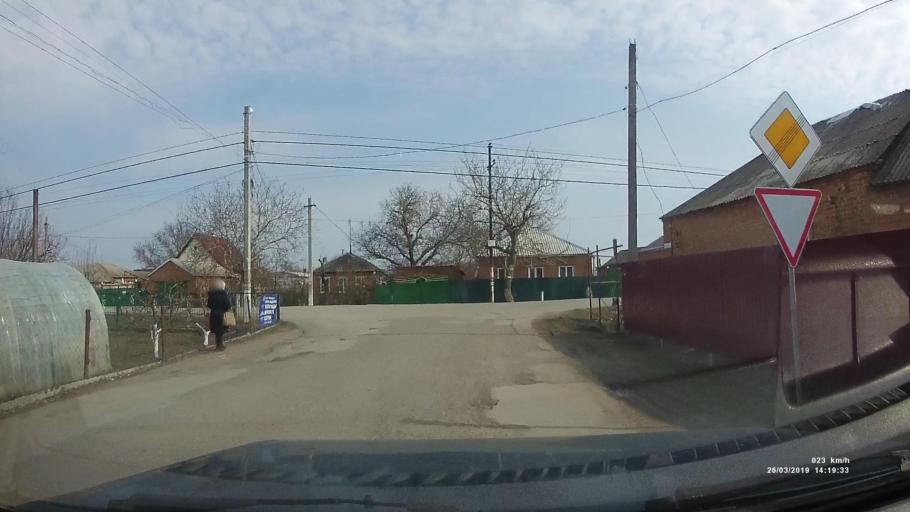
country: RU
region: Rostov
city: Novobessergenovka
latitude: 47.1891
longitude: 38.8700
